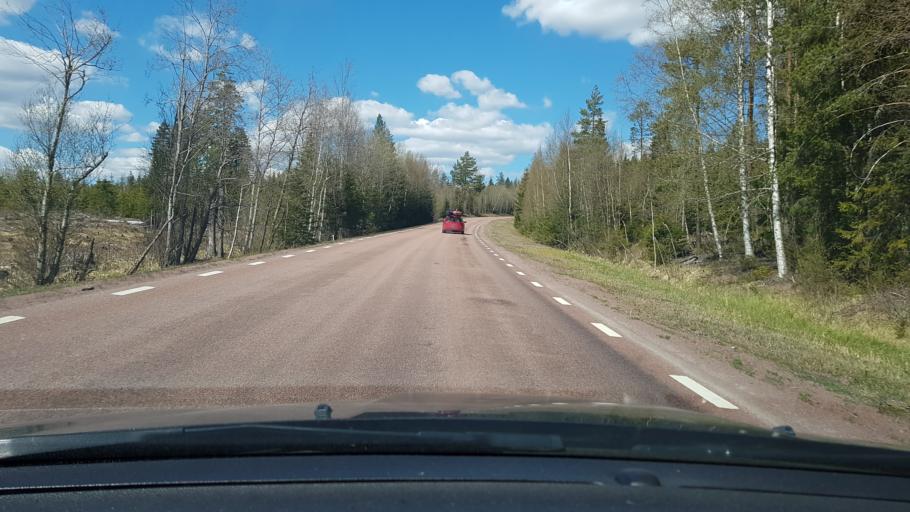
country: SE
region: Dalarna
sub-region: Alvdalens Kommun
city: AElvdalen
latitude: 61.1237
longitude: 13.9768
